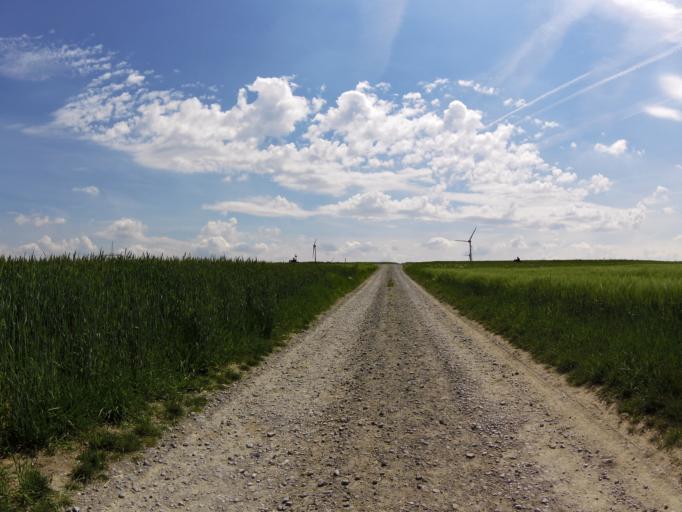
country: DE
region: Bavaria
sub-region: Regierungsbezirk Unterfranken
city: Theilheim
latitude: 49.7323
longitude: 10.0412
